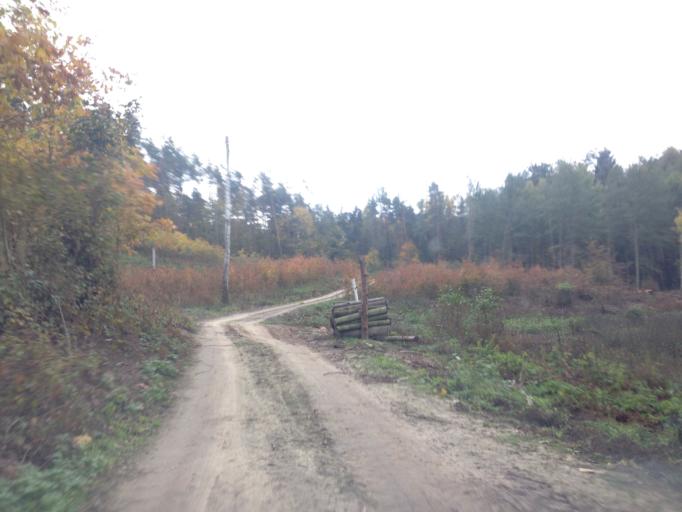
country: PL
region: Kujawsko-Pomorskie
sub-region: Powiat brodnicki
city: Gorzno
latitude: 53.2447
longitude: 19.6824
